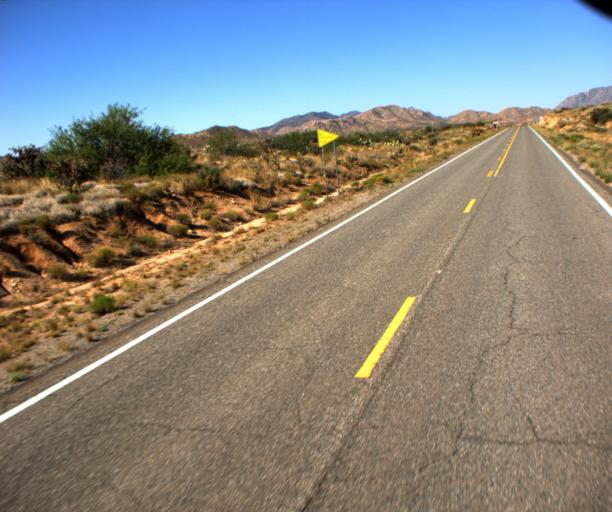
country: US
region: Arizona
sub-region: Graham County
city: Swift Trail Junction
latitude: 32.5853
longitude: -109.7017
